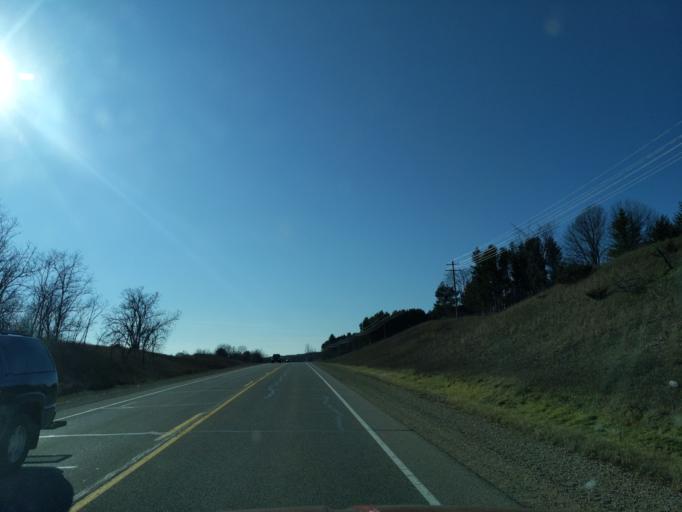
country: US
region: Wisconsin
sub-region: Waushara County
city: Wautoma
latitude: 44.1094
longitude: -89.2824
